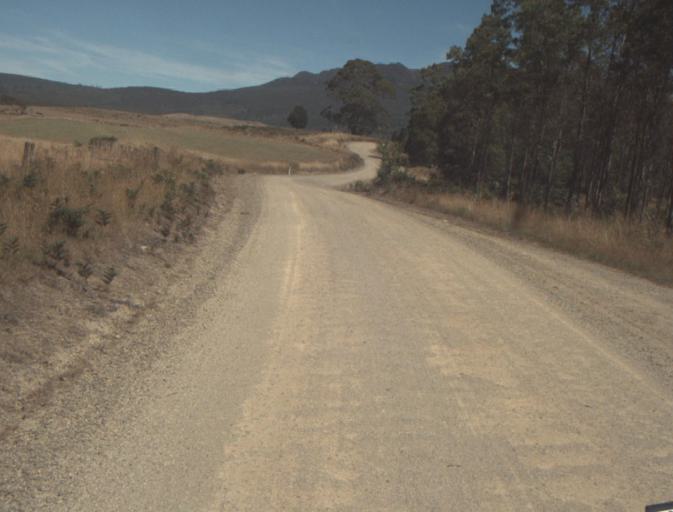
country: AU
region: Tasmania
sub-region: Dorset
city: Scottsdale
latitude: -41.3252
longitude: 147.4449
